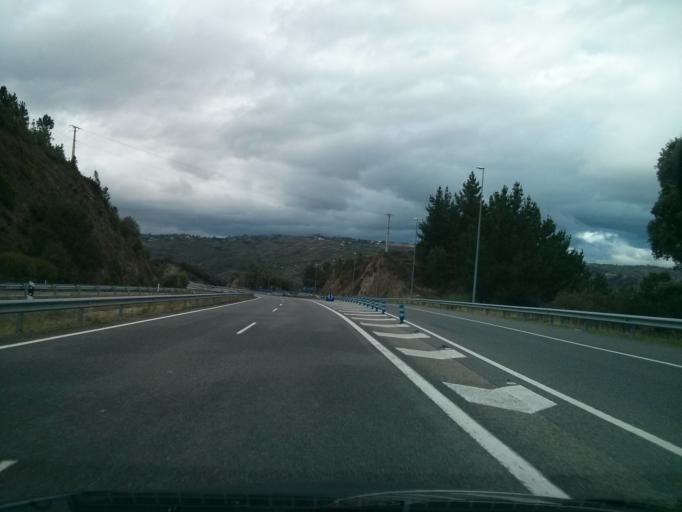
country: ES
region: Galicia
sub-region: Provincia de Ourense
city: Ourense
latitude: 42.3405
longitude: -7.8848
